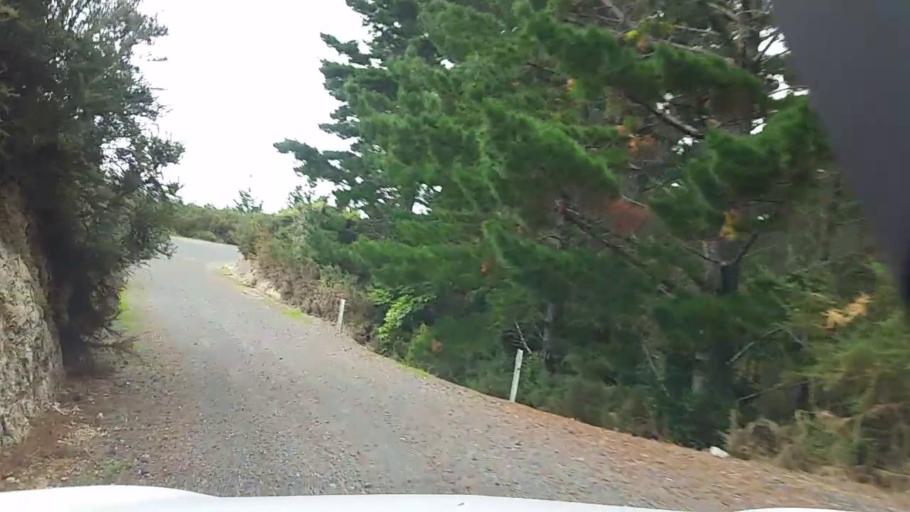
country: NZ
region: Northland
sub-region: Far North District
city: Kawakawa
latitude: -35.4619
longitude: 174.2634
